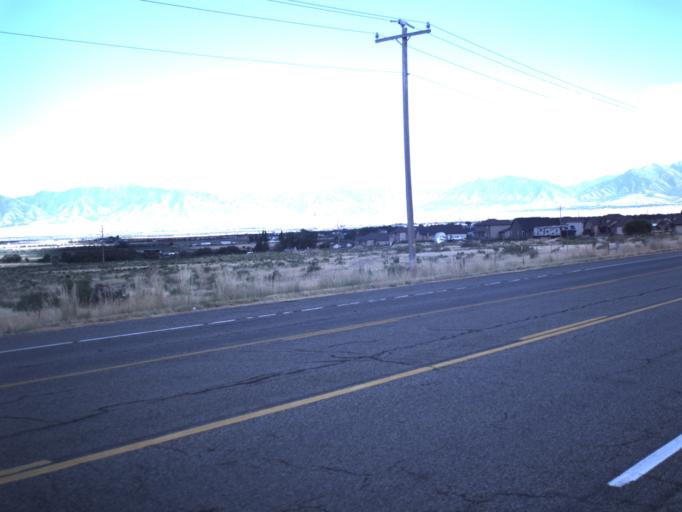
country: US
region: Utah
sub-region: Tooele County
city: Grantsville
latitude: 40.6228
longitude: -112.5055
